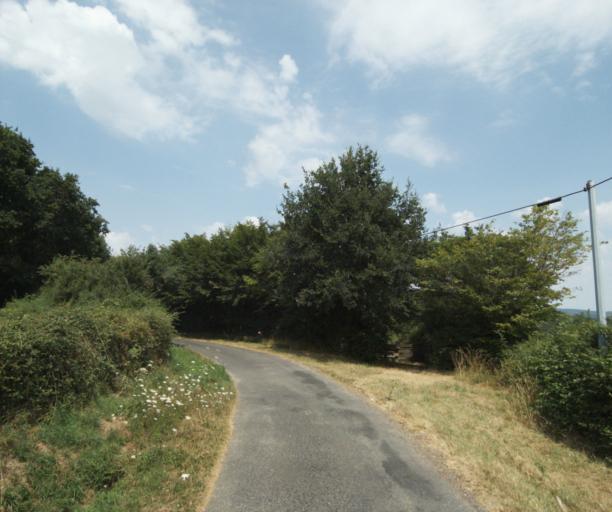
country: FR
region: Bourgogne
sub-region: Departement de Saone-et-Loire
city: Gueugnon
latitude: 46.6013
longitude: 4.0245
